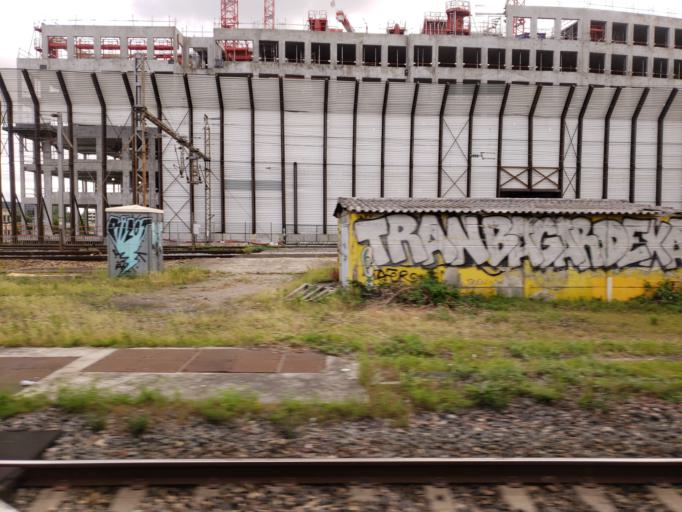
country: FR
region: Ile-de-France
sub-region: Paris
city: Saint-Ouen
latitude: 48.8979
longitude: 2.3547
